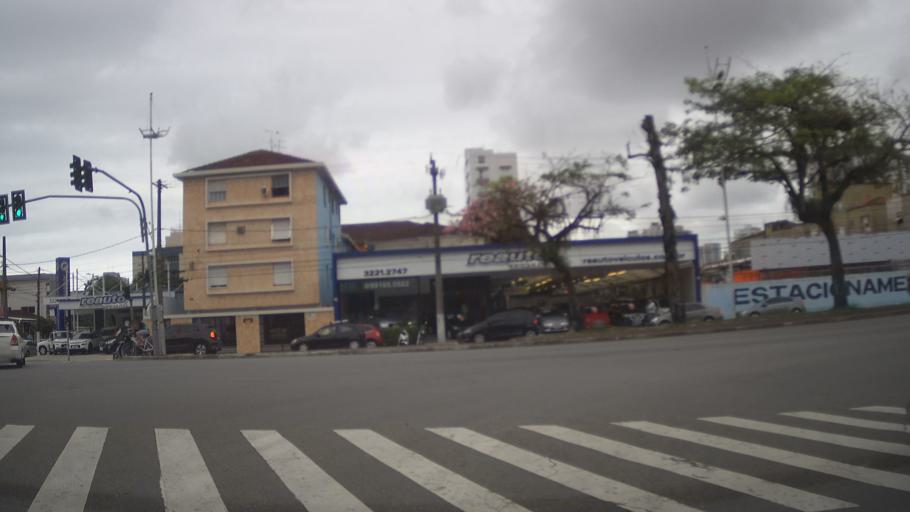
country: BR
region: Sao Paulo
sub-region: Santos
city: Santos
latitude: -23.9584
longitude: -46.3200
